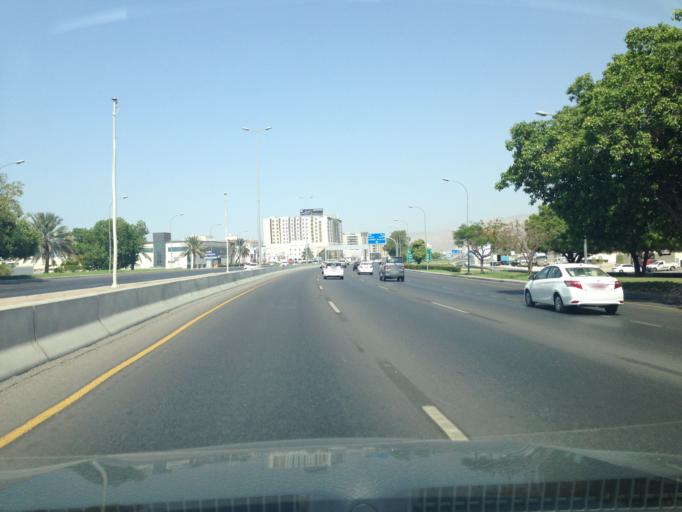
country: OM
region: Muhafazat Masqat
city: Bawshar
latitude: 23.5907
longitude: 58.3722
